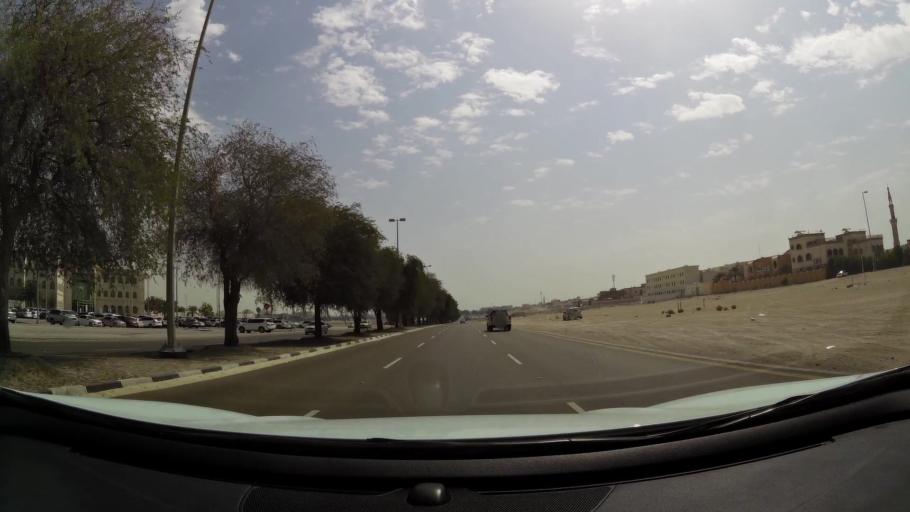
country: AE
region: Abu Dhabi
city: Abu Dhabi
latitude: 24.3140
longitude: 54.6096
